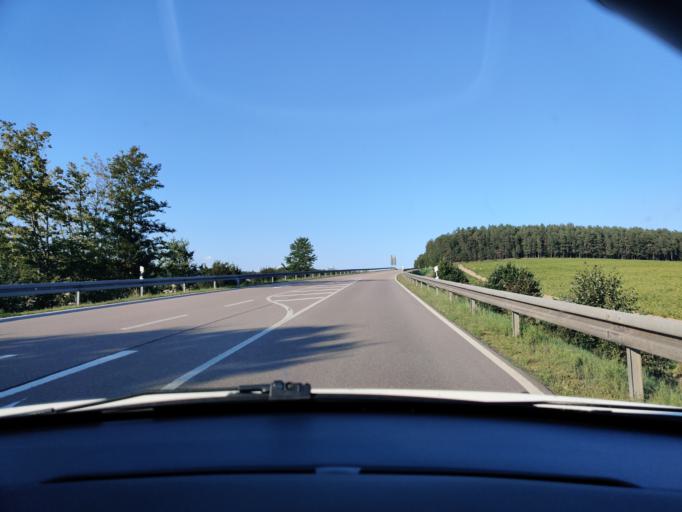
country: DE
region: Bavaria
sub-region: Upper Palatinate
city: Stulln
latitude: 49.4391
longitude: 12.1467
